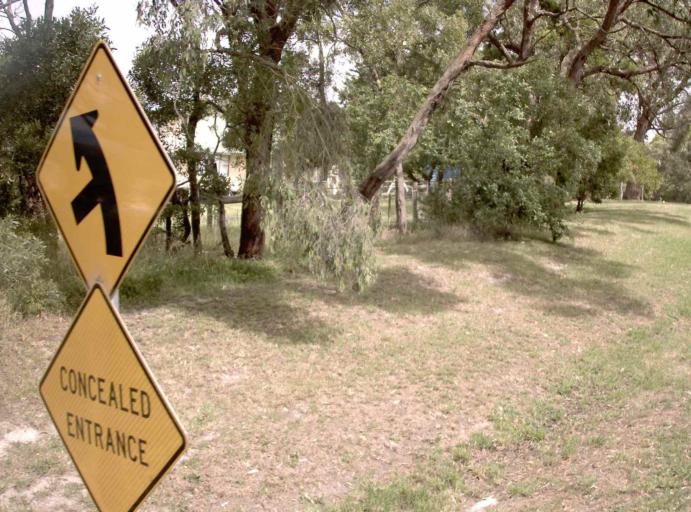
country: AU
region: Victoria
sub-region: Latrobe
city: Moe
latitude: -38.1002
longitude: 146.2374
